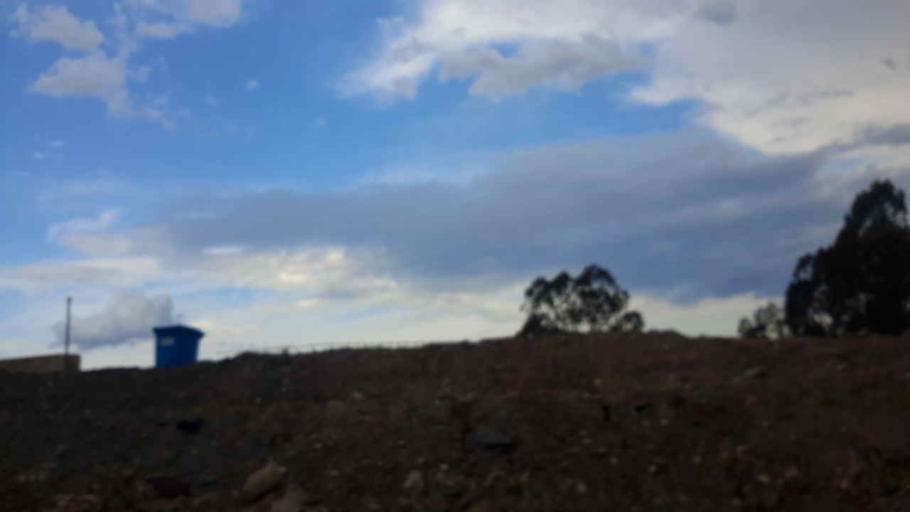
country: AU
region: New South Wales
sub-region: Penrith Municipality
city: Kingswood Park
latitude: -33.7879
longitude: 150.7017
